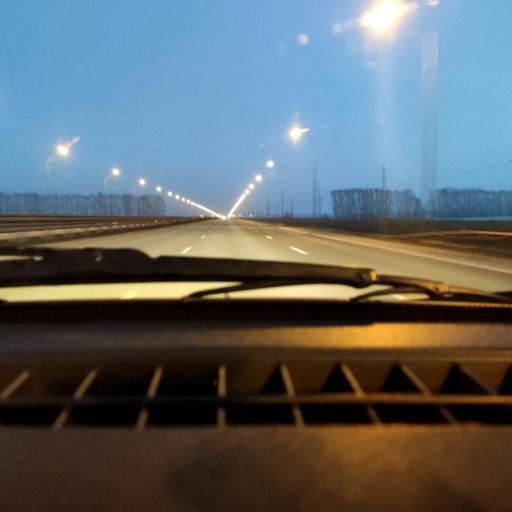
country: RU
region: Bashkortostan
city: Asanovo
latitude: 54.8902
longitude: 55.6555
